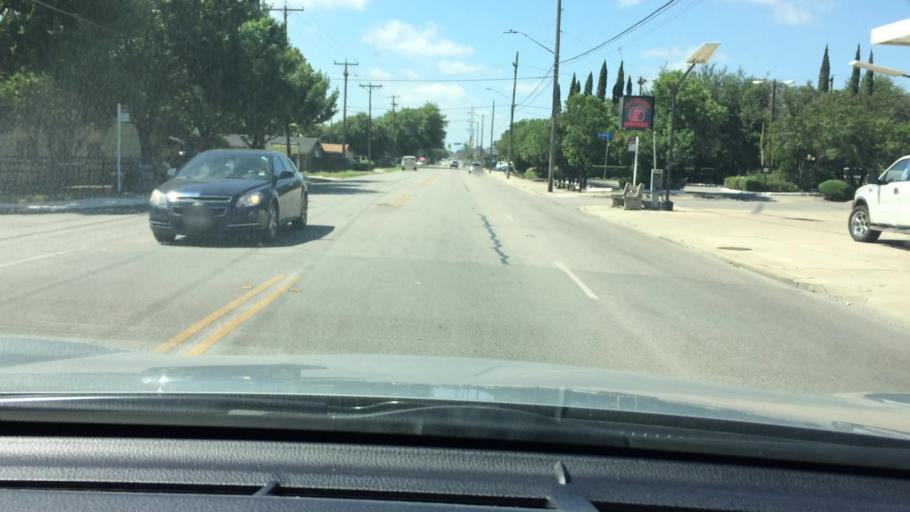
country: US
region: Texas
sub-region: Bexar County
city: Balcones Heights
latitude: 29.4968
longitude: -98.5351
